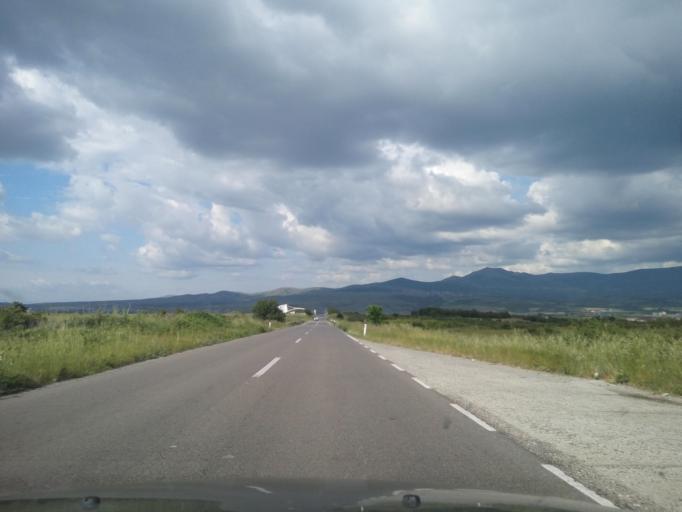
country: XK
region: Gjakova
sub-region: Komuna e Gjakoves
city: Gjakove
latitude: 42.4496
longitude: 20.4962
